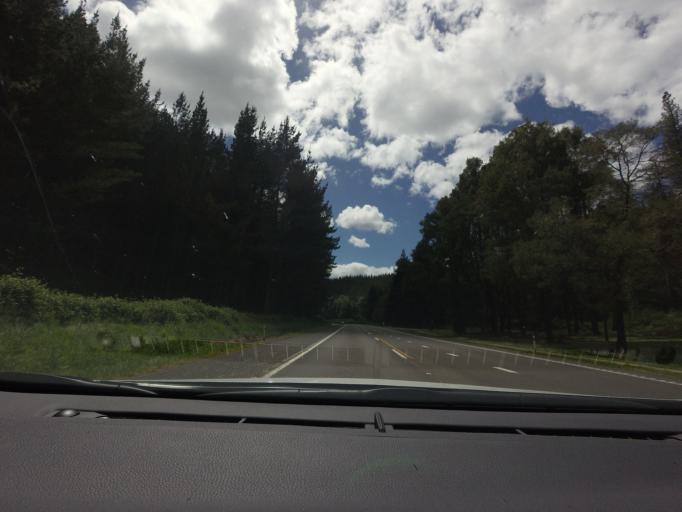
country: NZ
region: Bay of Plenty
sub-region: Rotorua District
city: Rotorua
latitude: -38.2310
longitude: 176.2978
